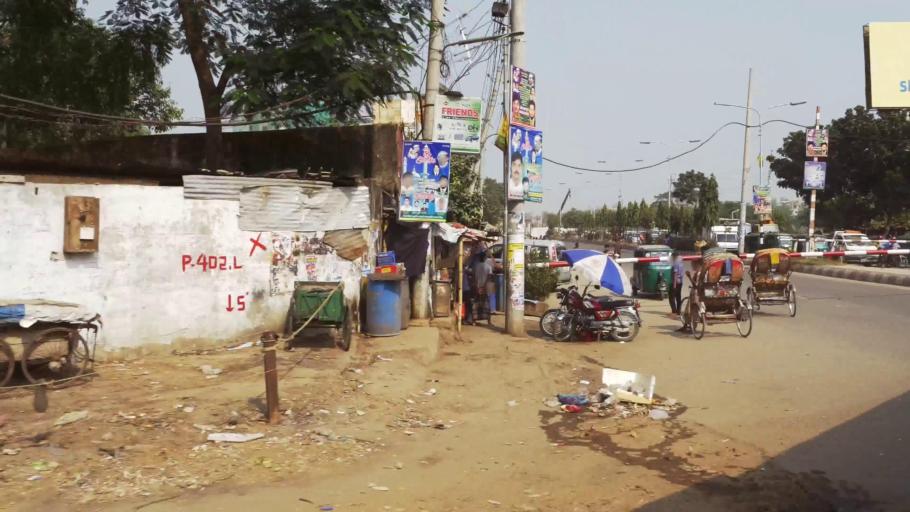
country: BD
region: Dhaka
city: Azimpur
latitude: 23.7566
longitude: 90.3943
